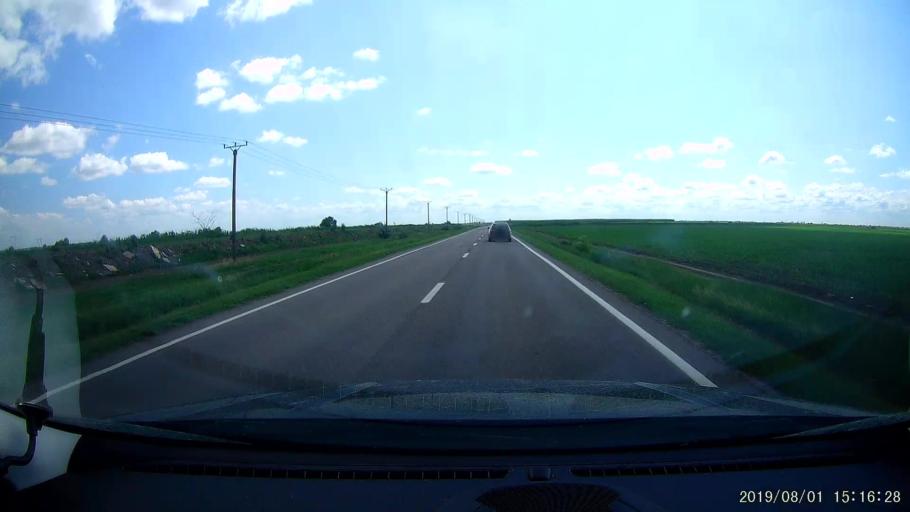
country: RO
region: Braila
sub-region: Comuna Unirea
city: Unirea
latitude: 45.1466
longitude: 27.8526
